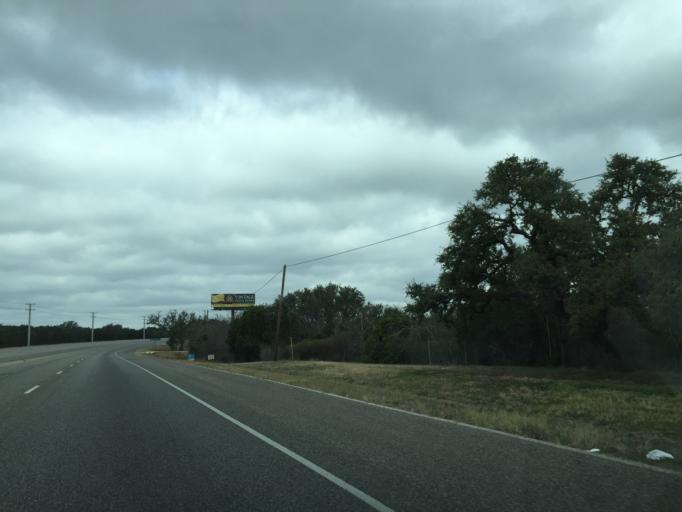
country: US
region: Texas
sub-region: Travis County
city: Briarcliff
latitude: 30.3480
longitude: -98.0568
